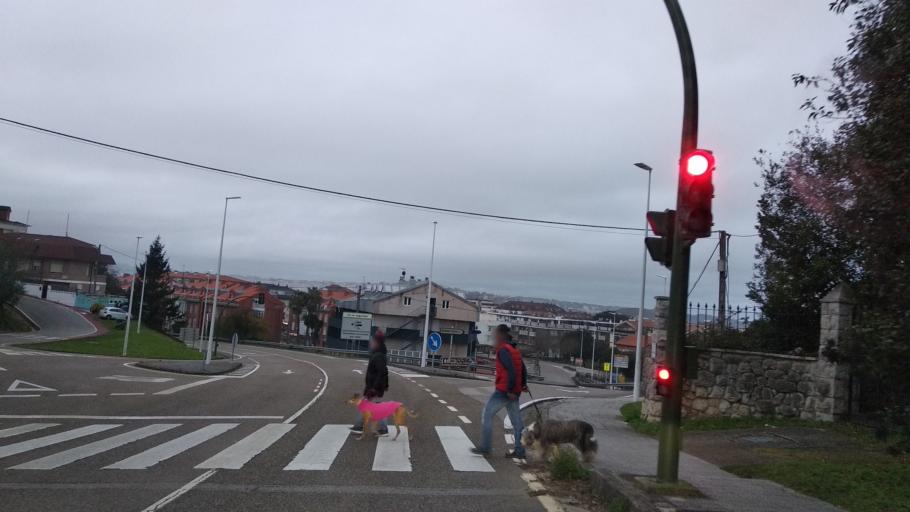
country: ES
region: Cantabria
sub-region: Provincia de Cantabria
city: Santander
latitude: 43.4532
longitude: -3.7406
